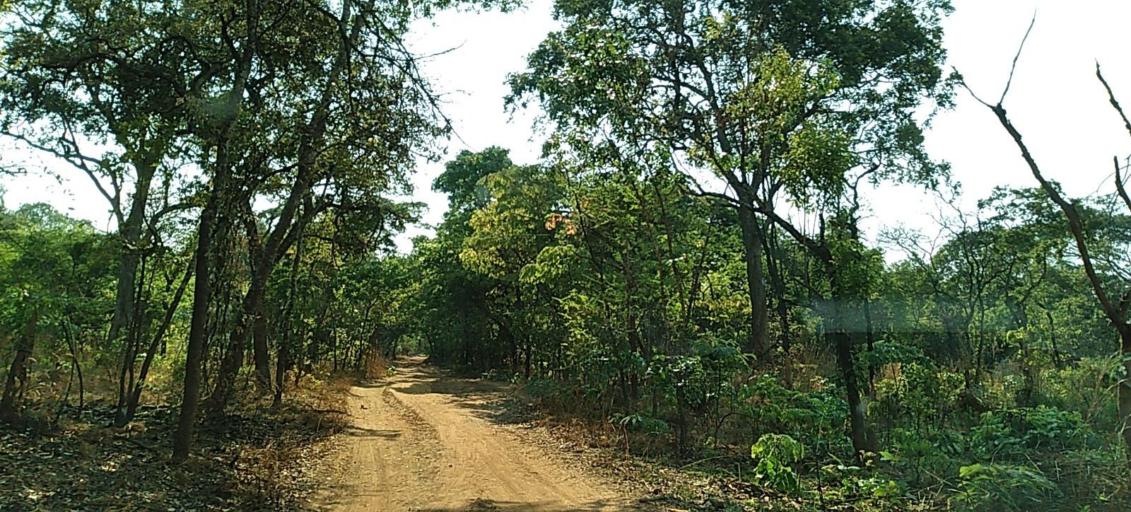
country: ZM
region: Copperbelt
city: Kalulushi
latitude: -13.0048
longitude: 27.7582
